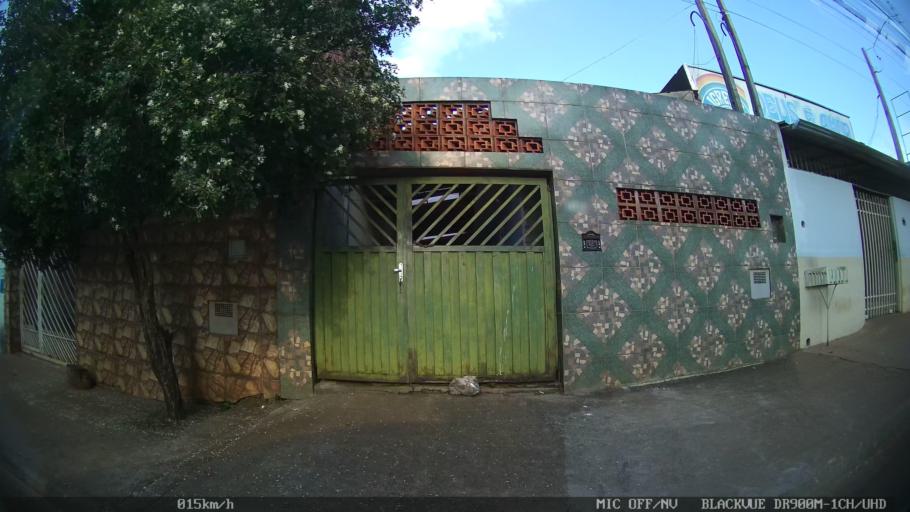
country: BR
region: Sao Paulo
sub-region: Hortolandia
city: Hortolandia
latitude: -22.8720
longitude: -47.1447
